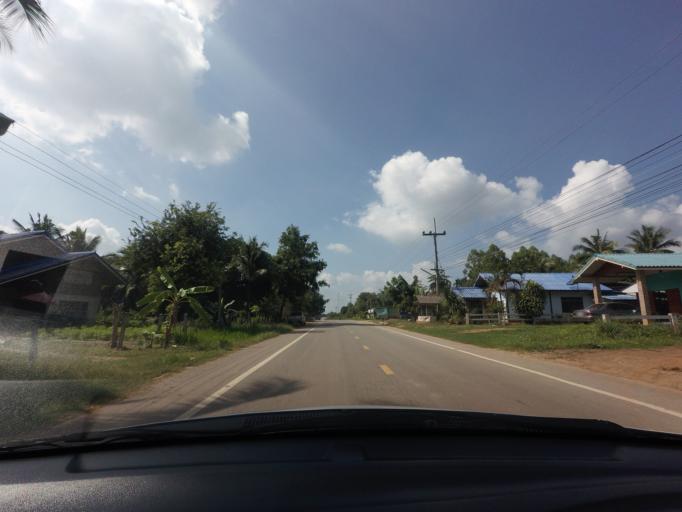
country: TH
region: Nakhon Ratchasima
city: Wang Nam Khiao
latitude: 14.4462
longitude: 101.6722
